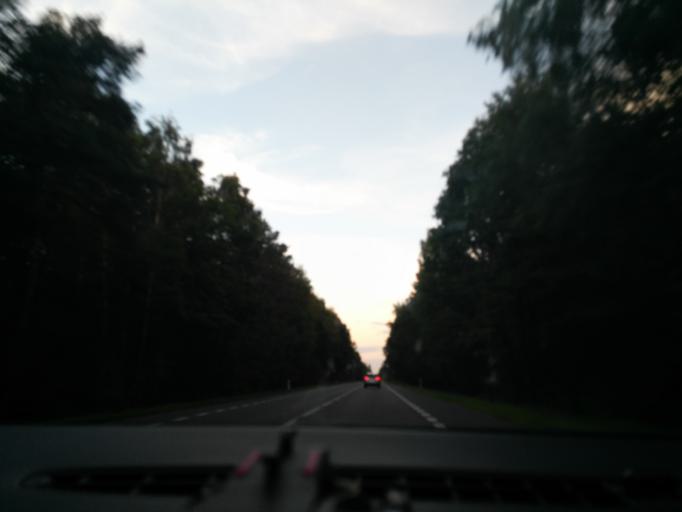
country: PL
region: Lublin Voivodeship
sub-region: Powiat radzynski
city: Borki
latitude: 51.7469
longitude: 22.5582
